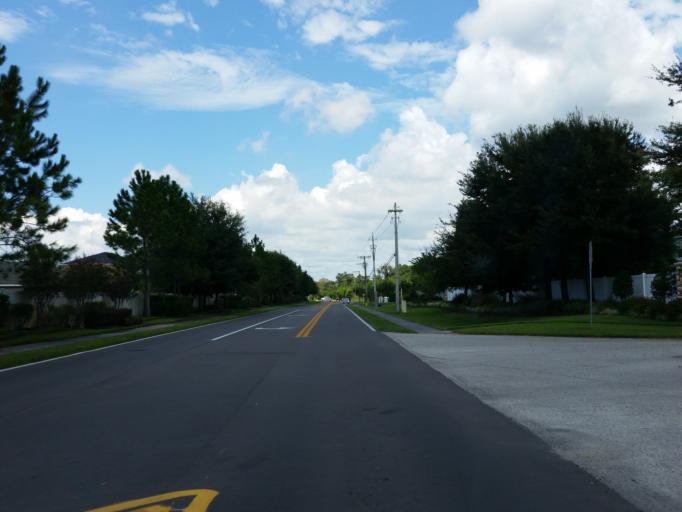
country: US
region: Florida
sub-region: Hillsborough County
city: Riverview
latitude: 27.8372
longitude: -82.3091
